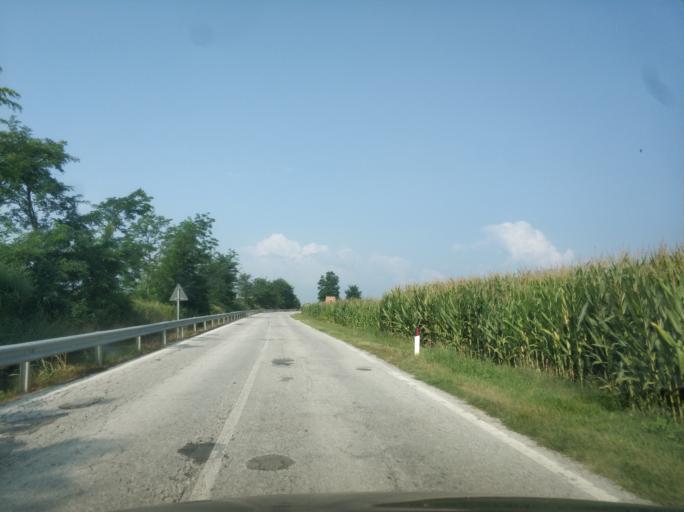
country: IT
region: Piedmont
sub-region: Provincia di Cuneo
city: Montanera
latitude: 44.5139
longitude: 7.6664
